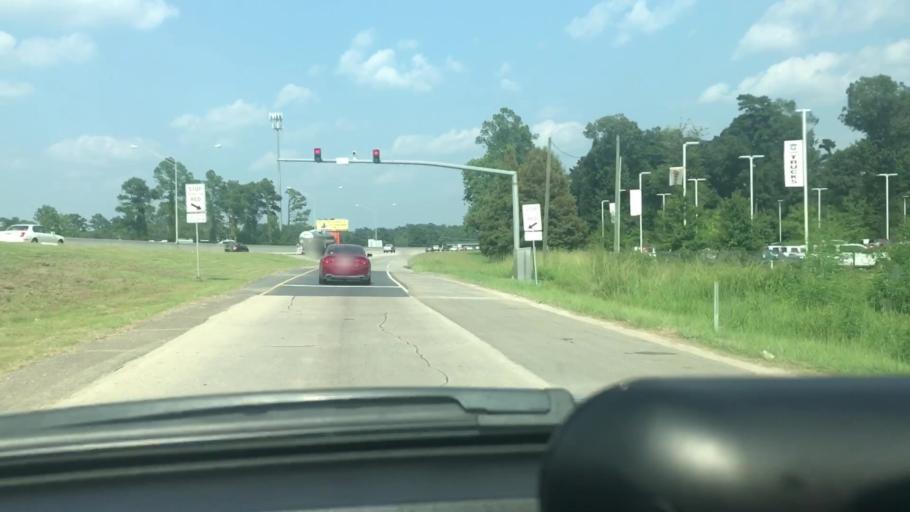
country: US
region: Louisiana
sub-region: Livingston Parish
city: Denham Springs
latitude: 30.4552
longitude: -90.9541
